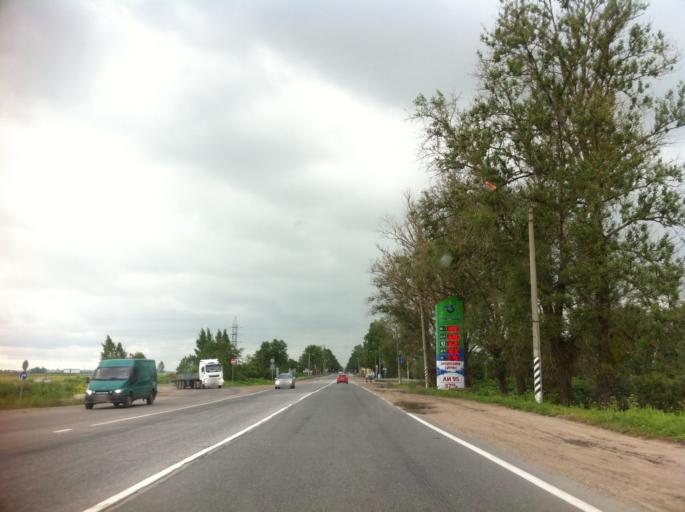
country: RU
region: Leningrad
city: Mariyenburg
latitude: 59.5194
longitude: 30.0654
